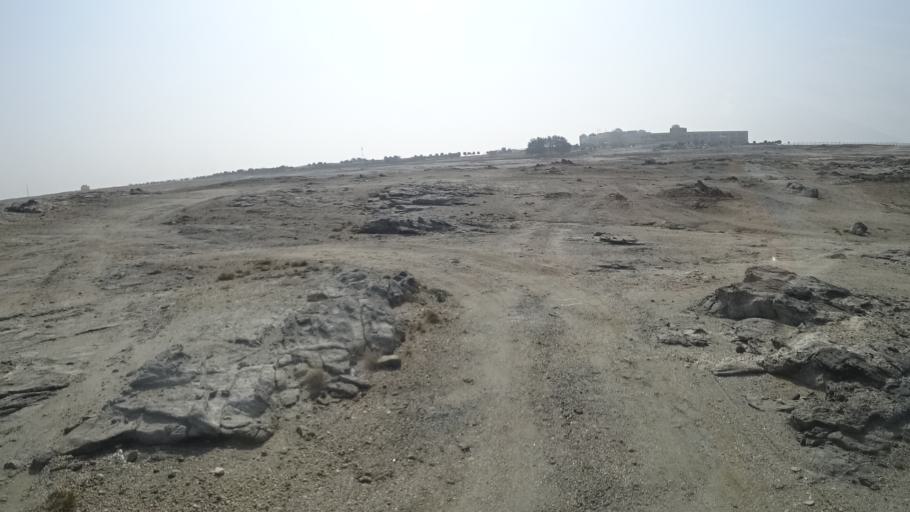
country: OM
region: Zufar
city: Salalah
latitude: 16.9596
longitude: 54.7330
